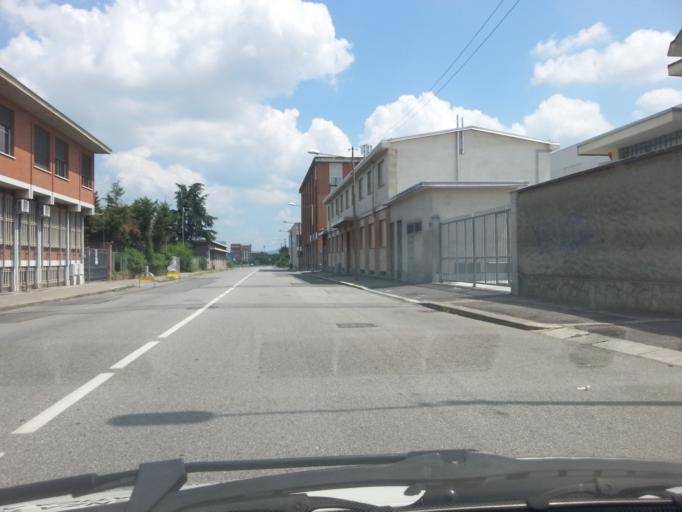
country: IT
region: Piedmont
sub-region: Provincia di Torino
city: Venaria Reale
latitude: 45.1081
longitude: 7.6679
